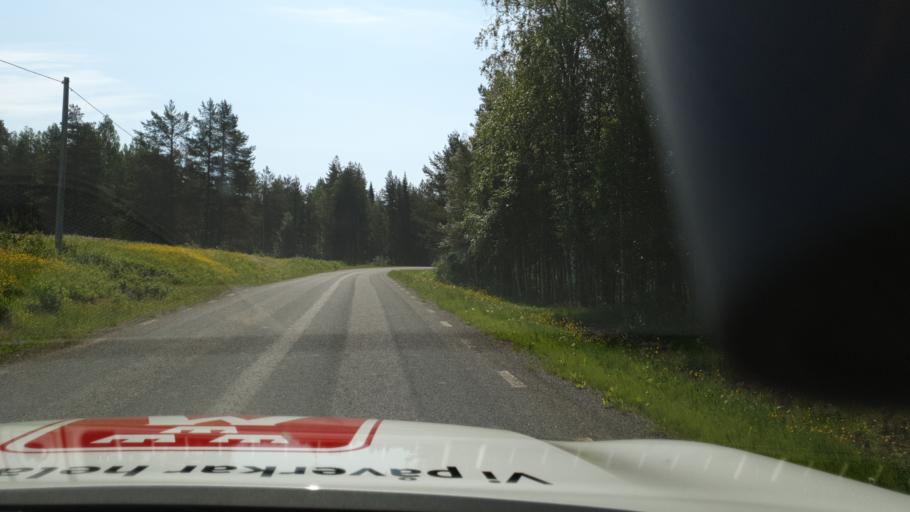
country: SE
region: Vaesterbotten
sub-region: Skelleftea Kommun
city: Langsele
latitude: 65.0153
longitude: 20.0782
